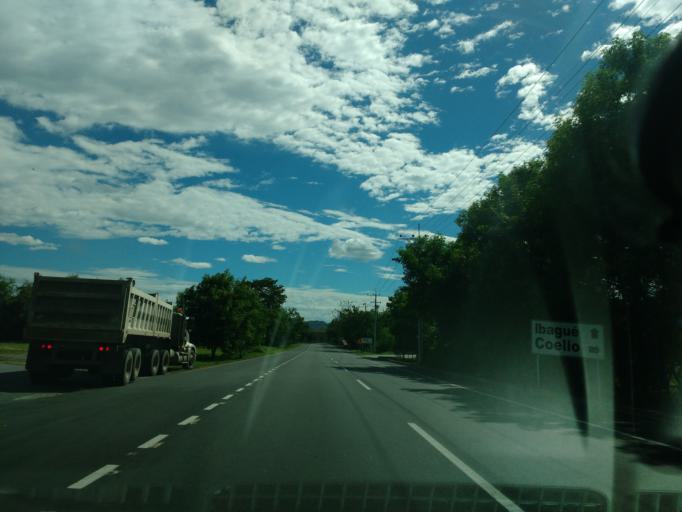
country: CO
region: Tolima
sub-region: Flandes
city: Flandes
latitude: 4.2442
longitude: -74.8847
